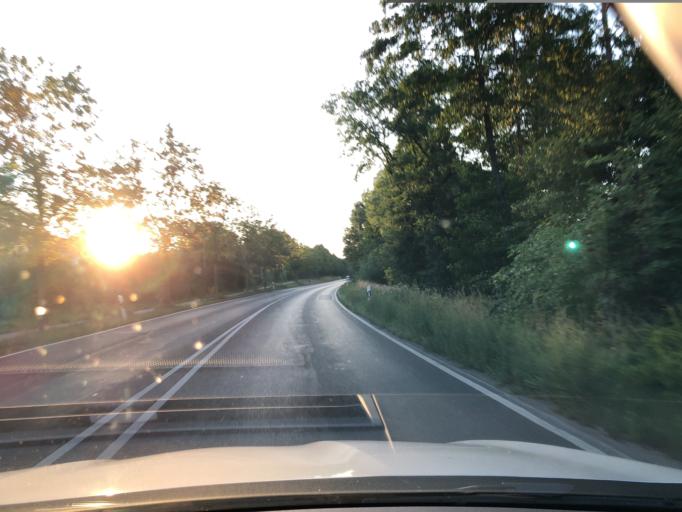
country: DE
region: Bavaria
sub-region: Upper Palatinate
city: Sulzbach-Rosenberg
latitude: 49.4903
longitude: 11.7637
